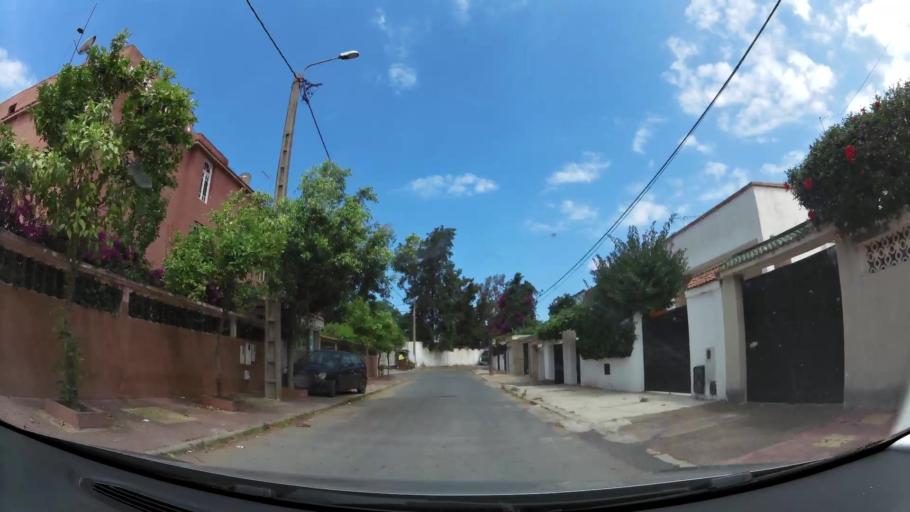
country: MA
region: Gharb-Chrarda-Beni Hssen
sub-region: Kenitra Province
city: Kenitra
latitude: 34.2551
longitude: -6.6020
